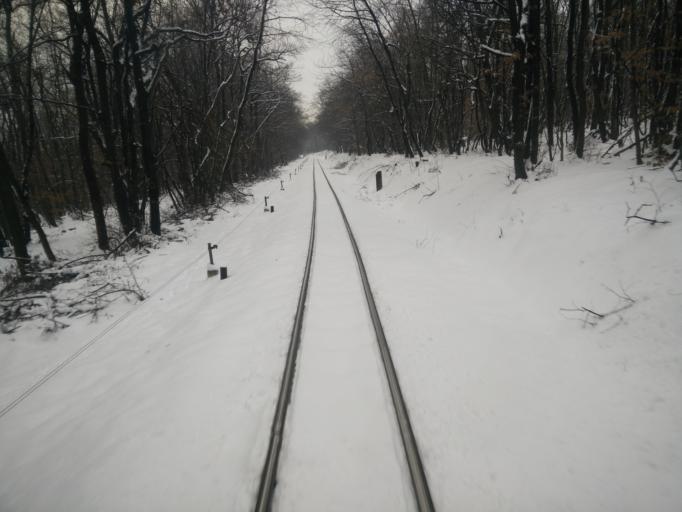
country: HU
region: Pest
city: Budakeszi
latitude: 47.5078
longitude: 18.9547
